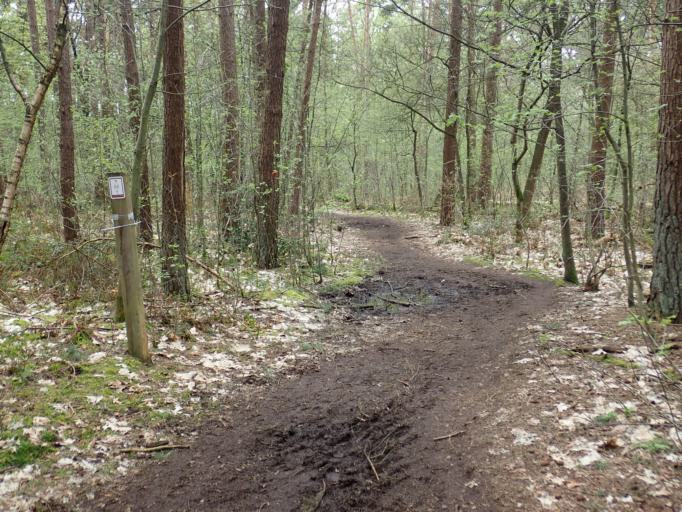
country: BE
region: Flanders
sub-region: Provincie Antwerpen
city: Lille
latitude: 51.2175
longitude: 4.8331
